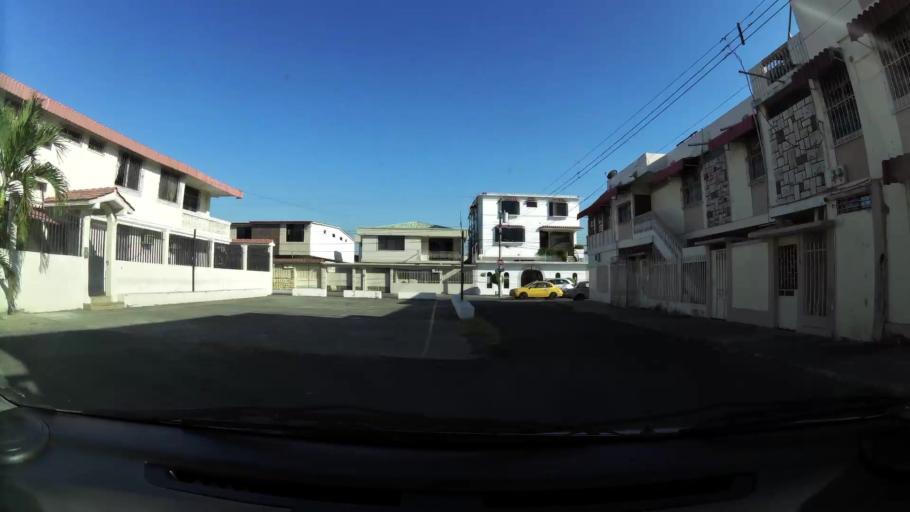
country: EC
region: Guayas
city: Eloy Alfaro
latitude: -2.1693
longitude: -79.8885
